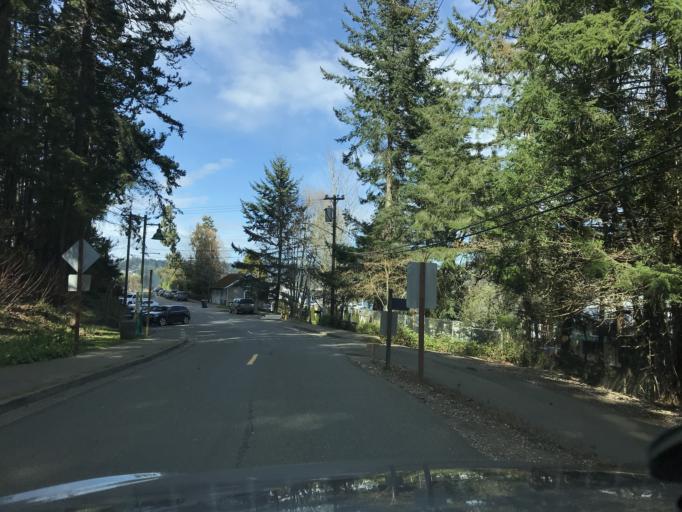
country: US
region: Washington
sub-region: Pierce County
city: Gig Harbor
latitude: 47.3277
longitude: -122.5776
